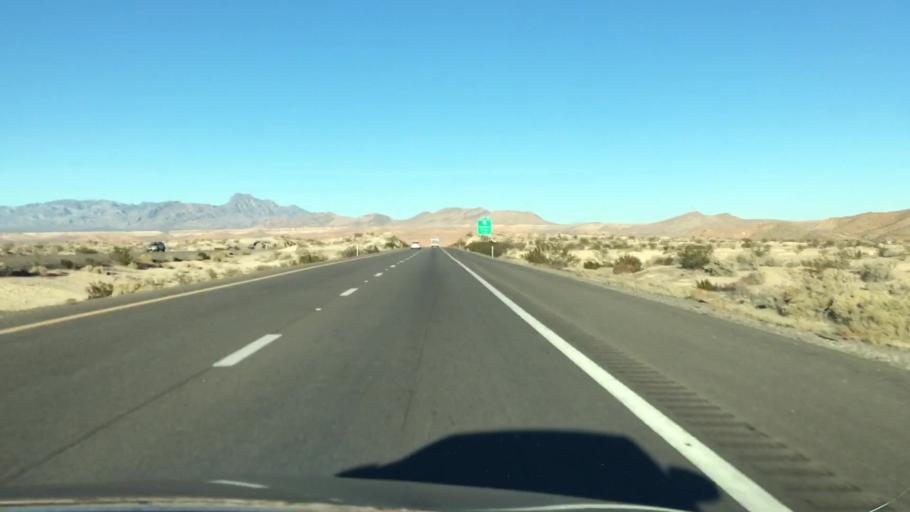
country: US
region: Nevada
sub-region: Clark County
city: Moapa Town
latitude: 36.6467
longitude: -114.5883
